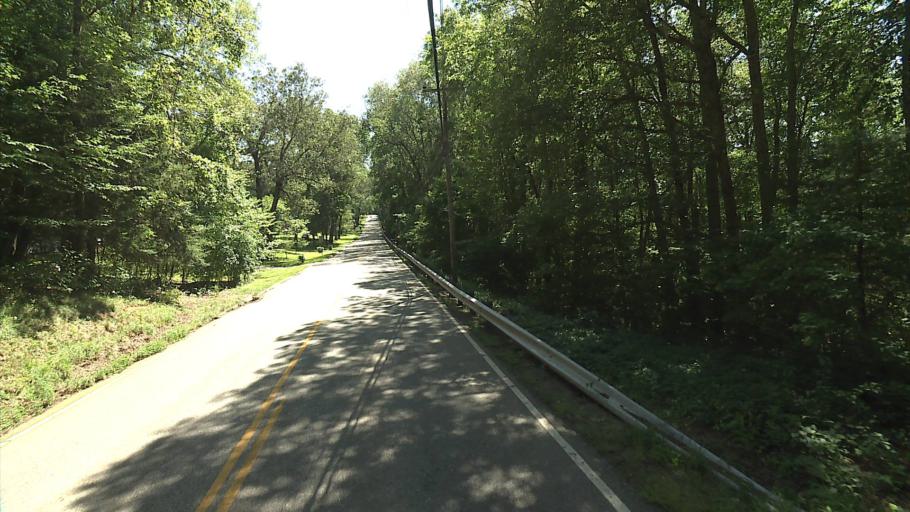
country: US
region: Connecticut
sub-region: New London County
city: Baltic
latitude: 41.6313
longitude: -72.0852
